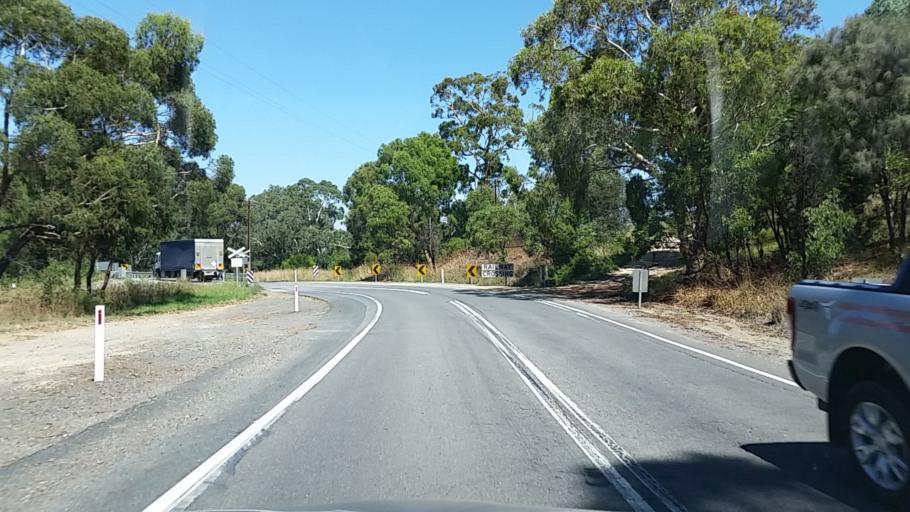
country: AU
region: South Australia
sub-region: Mount Barker
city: Little Hampton
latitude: -35.0283
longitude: 138.8608
